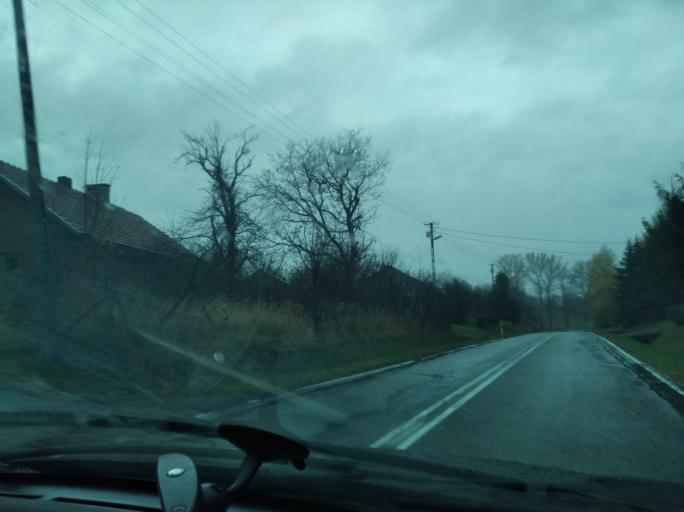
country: PL
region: Subcarpathian Voivodeship
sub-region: Powiat lancucki
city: Albigowa
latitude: 50.0072
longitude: 22.2143
